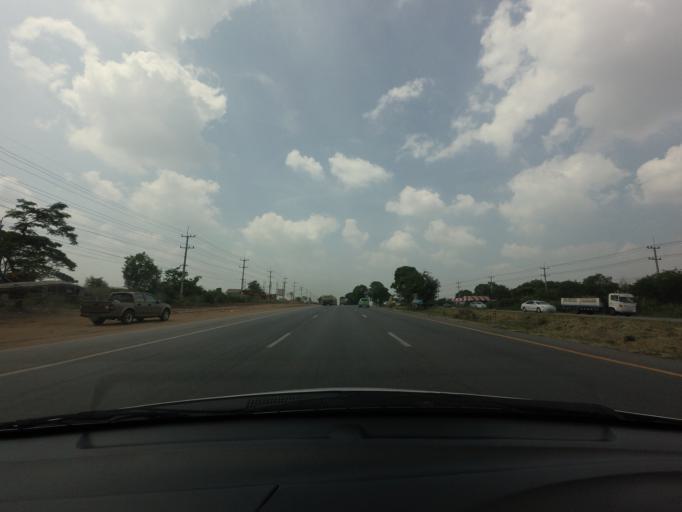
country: TH
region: Nakhon Ratchasima
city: Pak Chong
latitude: 14.6678
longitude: 101.4395
